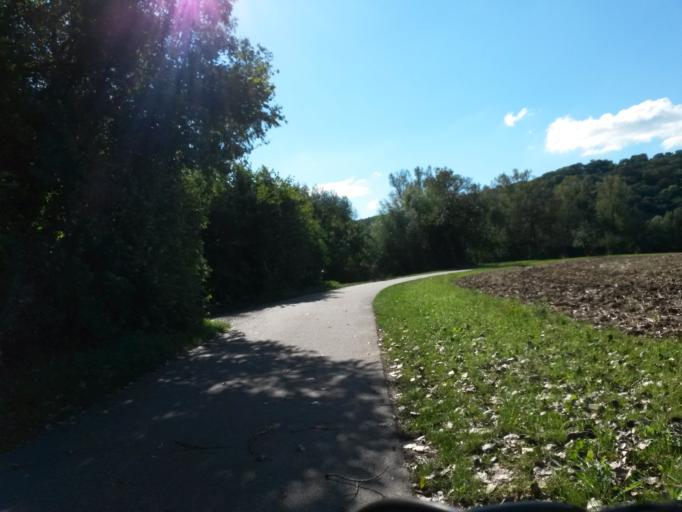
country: DE
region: Baden-Wuerttemberg
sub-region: Regierungsbezirk Stuttgart
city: Markgroningen
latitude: 48.9292
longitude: 9.0804
